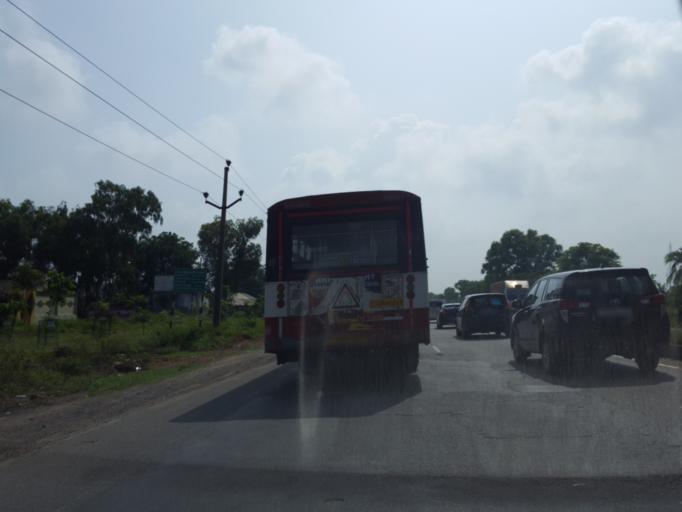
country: IN
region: Telangana
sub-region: Rangareddi
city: Ghatkesar
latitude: 17.3062
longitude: 78.7272
